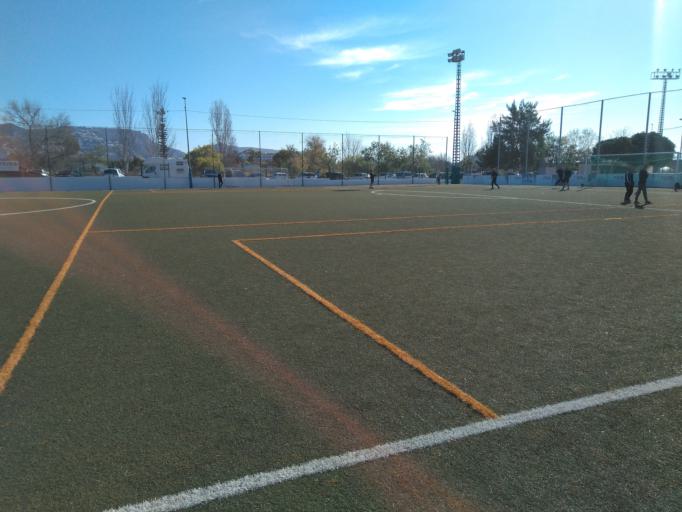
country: ES
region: Valencia
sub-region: Provincia de Alicante
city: Altea
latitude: 38.6064
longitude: -0.0442
